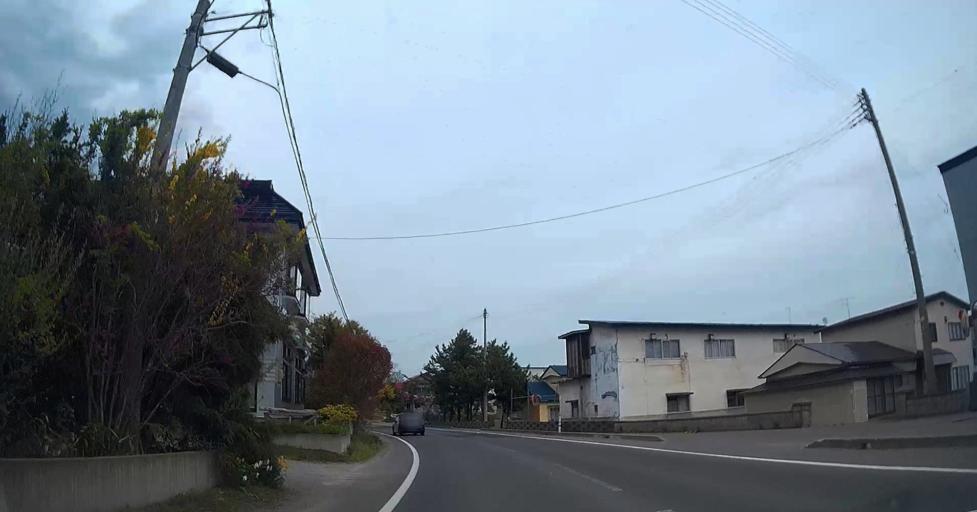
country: JP
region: Aomori
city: Shimokizukuri
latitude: 40.9708
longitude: 140.3678
